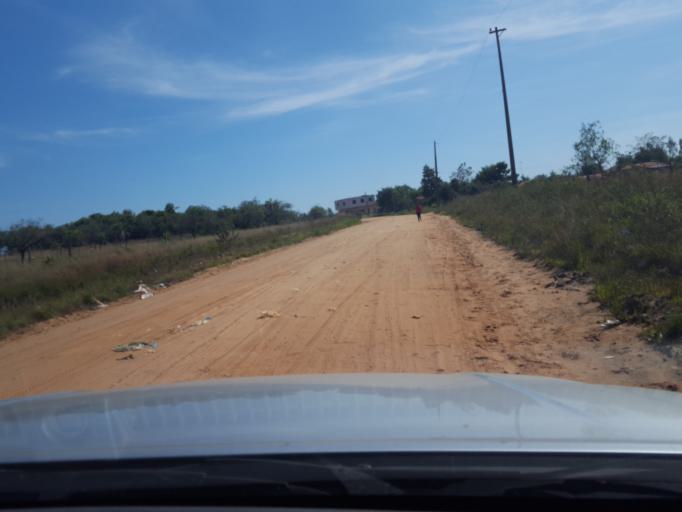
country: PY
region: Cordillera
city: Tobati
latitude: -25.2559
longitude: -57.1000
